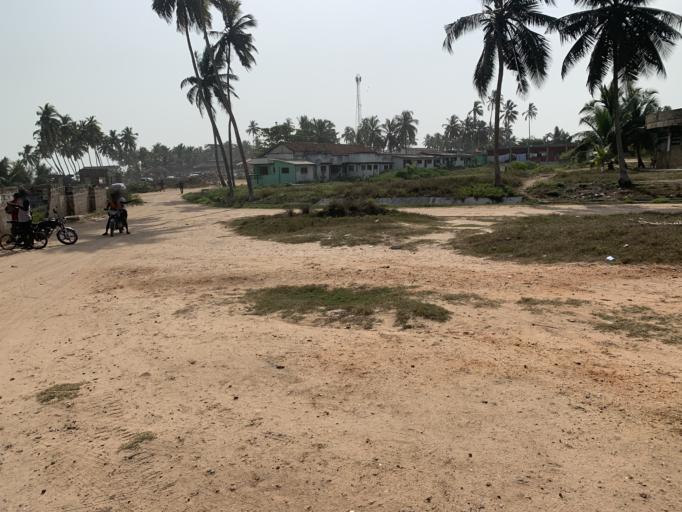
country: GH
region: Central
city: Winneba
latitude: 5.3316
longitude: -0.6260
